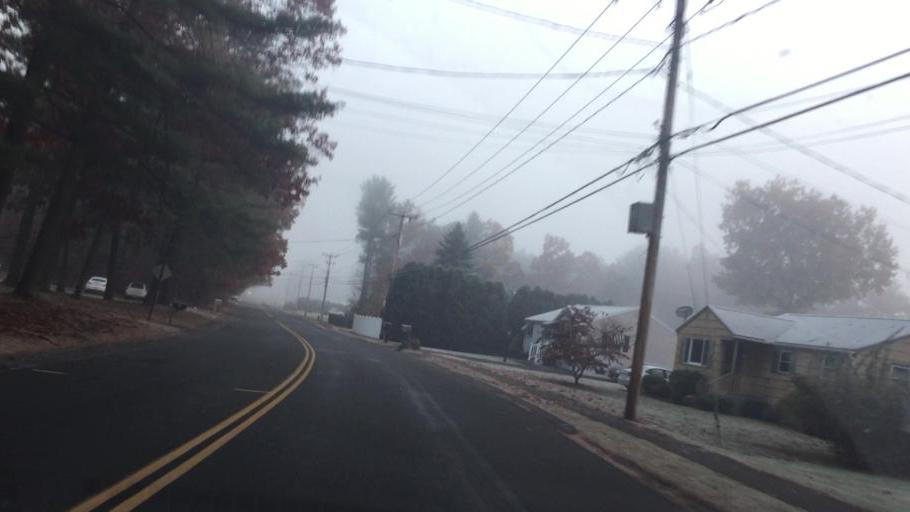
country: US
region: Massachusetts
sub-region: Hampshire County
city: Southampton
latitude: 42.2253
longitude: -72.6869
